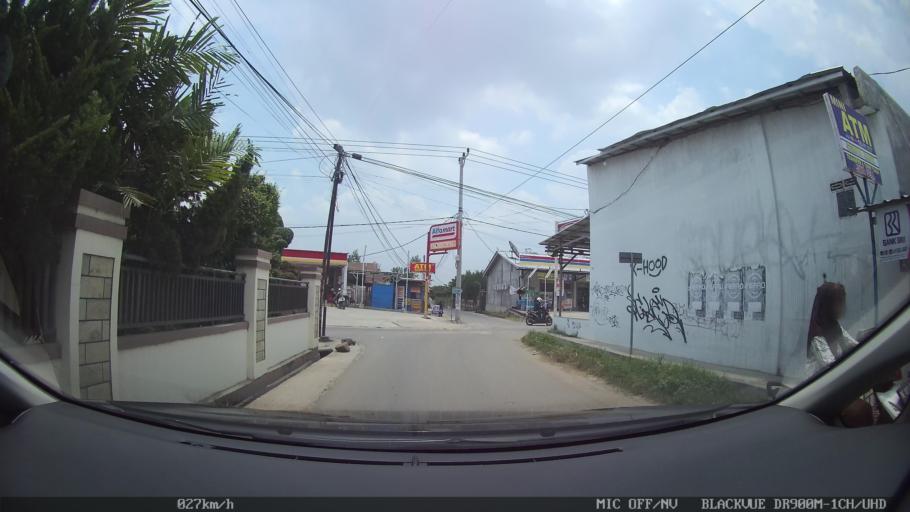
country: ID
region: Lampung
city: Pringsewu
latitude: -5.3508
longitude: 104.9794
